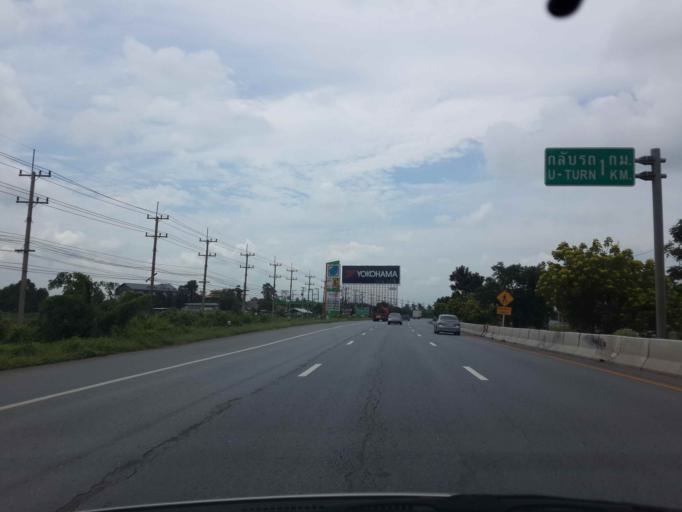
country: TH
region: Ratchaburi
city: Pak Tho
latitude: 13.3460
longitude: 99.8864
